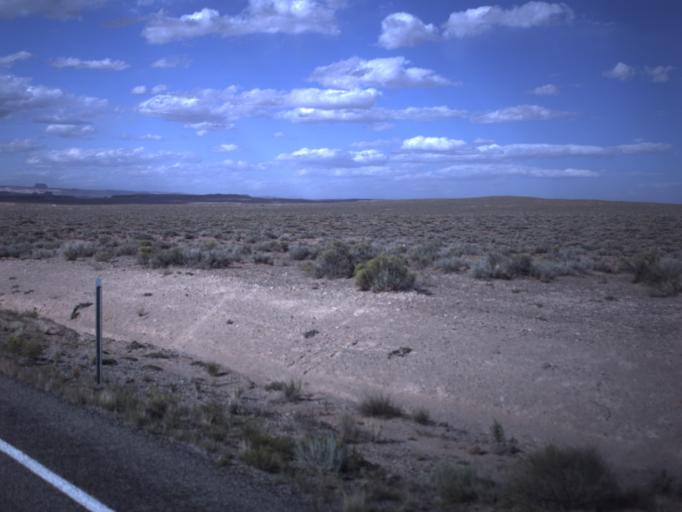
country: US
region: Utah
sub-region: Emery County
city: Ferron
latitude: 38.3452
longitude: -110.6926
